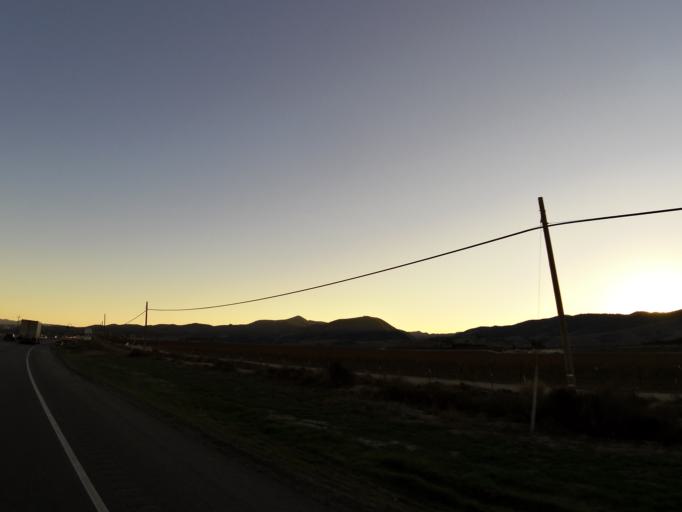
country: US
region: California
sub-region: Monterey County
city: King City
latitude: 36.2525
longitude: -121.1767
